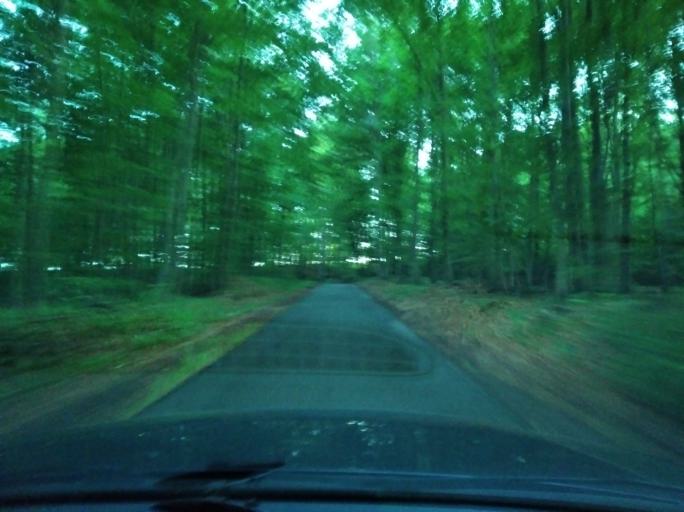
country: PL
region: Subcarpathian Voivodeship
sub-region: Powiat strzyzowski
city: Czudec
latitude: 49.9225
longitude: 21.8377
